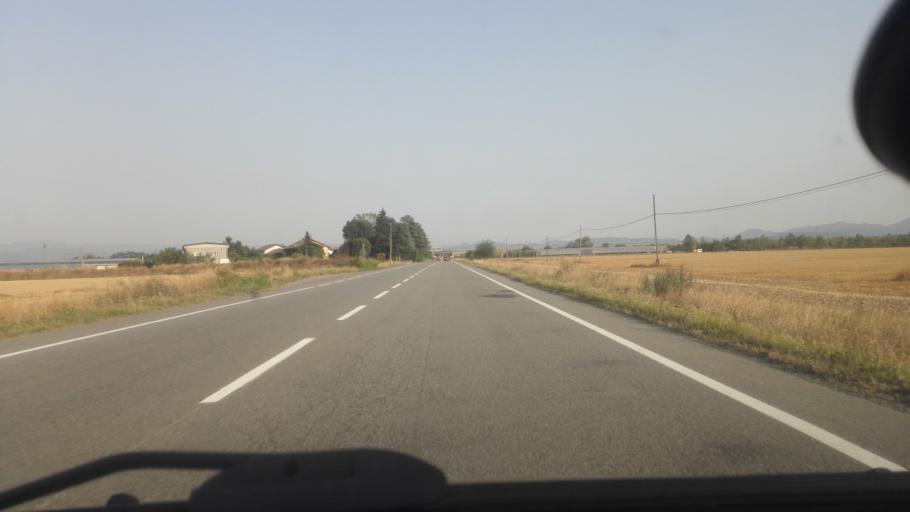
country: IT
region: Piedmont
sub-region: Provincia di Alessandria
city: Pozzolo Formigaro
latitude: 44.8141
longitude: 8.7603
